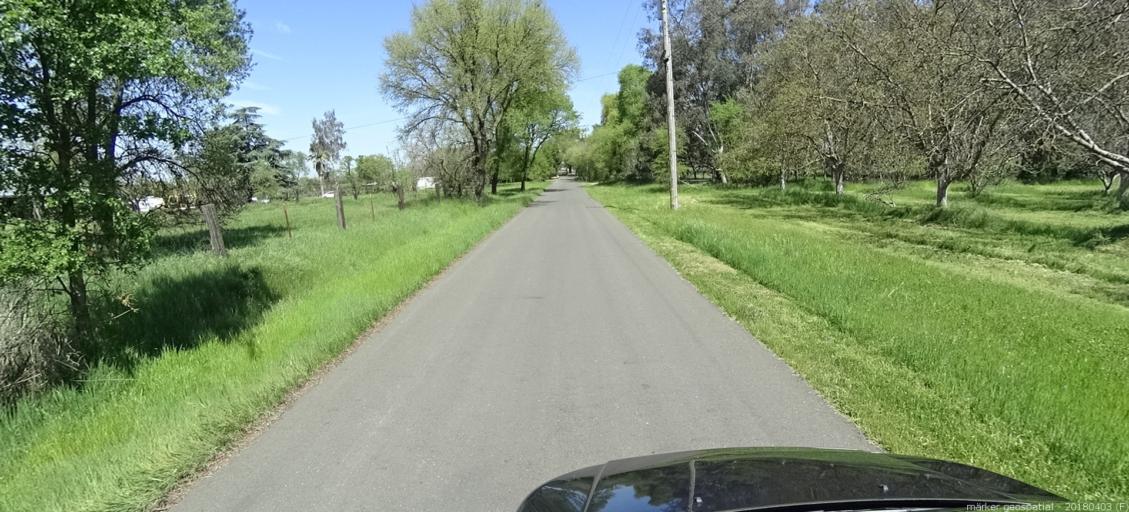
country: US
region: California
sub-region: Sacramento County
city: Wilton
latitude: 38.4038
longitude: -121.2780
